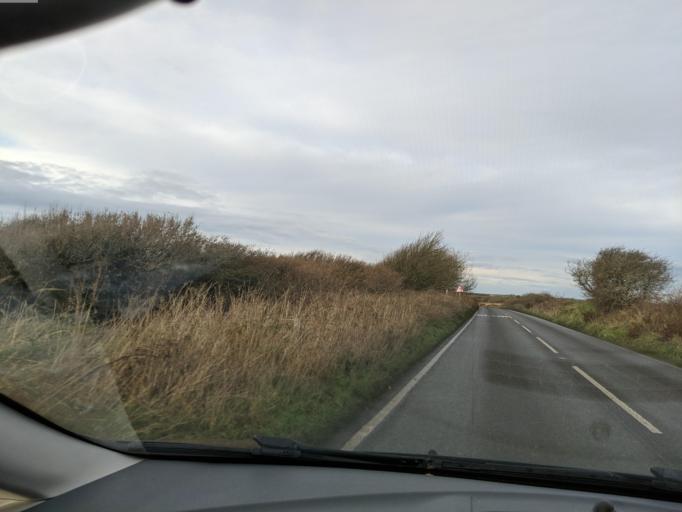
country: GB
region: England
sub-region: Cornwall
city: Jacobstow
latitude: 50.6888
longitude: -4.6153
